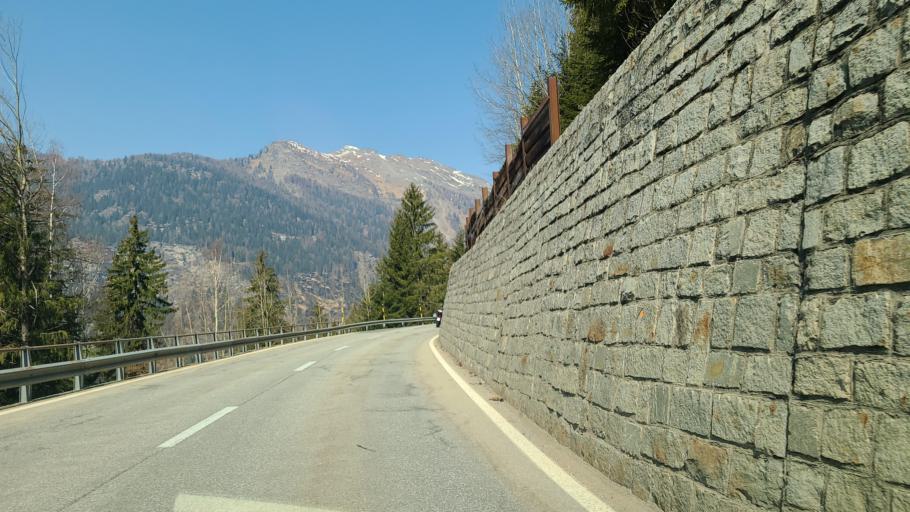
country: CH
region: Grisons
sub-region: Bernina District
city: Poschiavo
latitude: 46.3612
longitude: 10.0781
